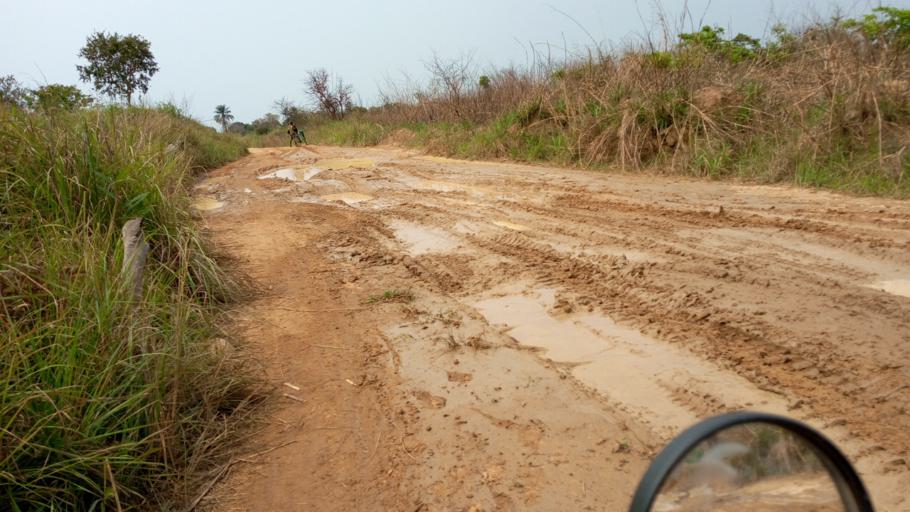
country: CD
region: Bandundu
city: Bandundu
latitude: -3.4824
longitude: 17.7856
